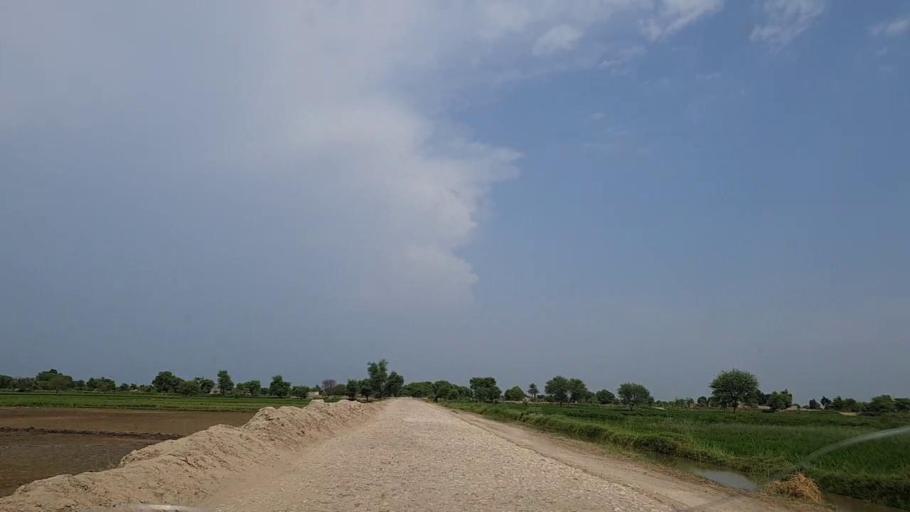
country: PK
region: Sindh
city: Khanpur
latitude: 27.8469
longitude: 69.4529
